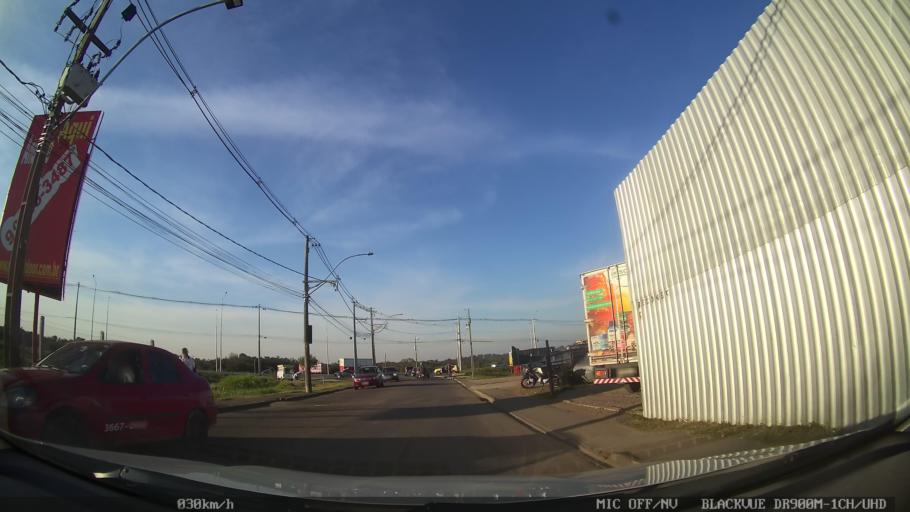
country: BR
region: Parana
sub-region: Pinhais
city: Pinhais
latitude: -25.4462
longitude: -49.1397
